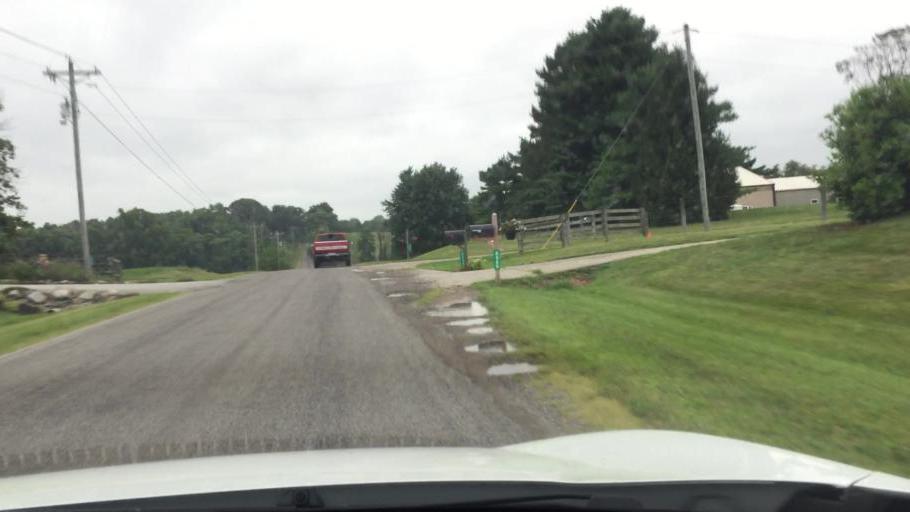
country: US
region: Ohio
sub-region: Champaign County
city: Mechanicsburg
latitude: 40.0408
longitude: -83.5910
